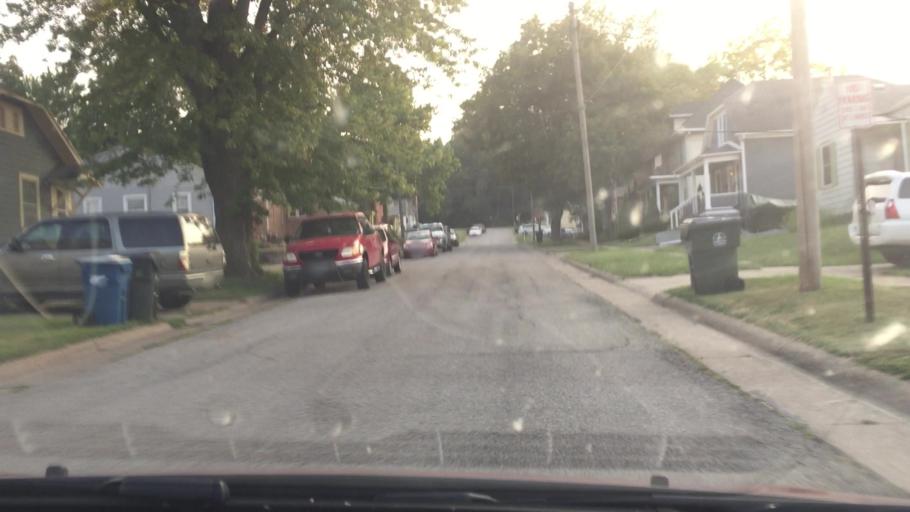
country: US
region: Iowa
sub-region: Muscatine County
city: Muscatine
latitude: 41.4282
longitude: -91.0511
